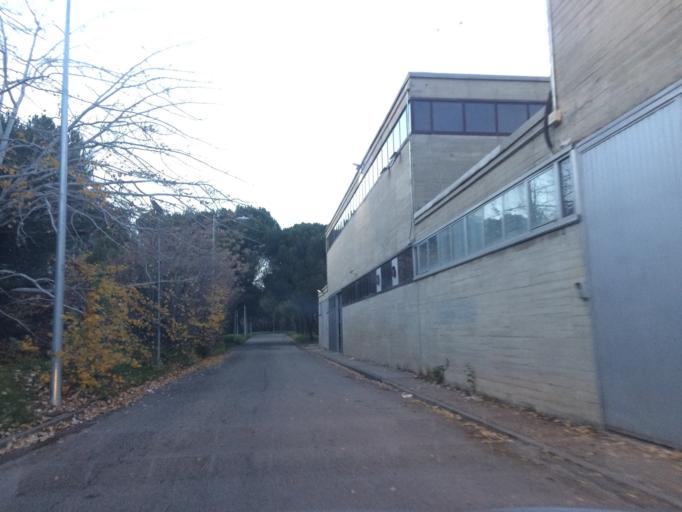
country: ES
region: Madrid
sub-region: Provincia de Madrid
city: Moncloa-Aravaca
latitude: 40.4462
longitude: -3.7332
